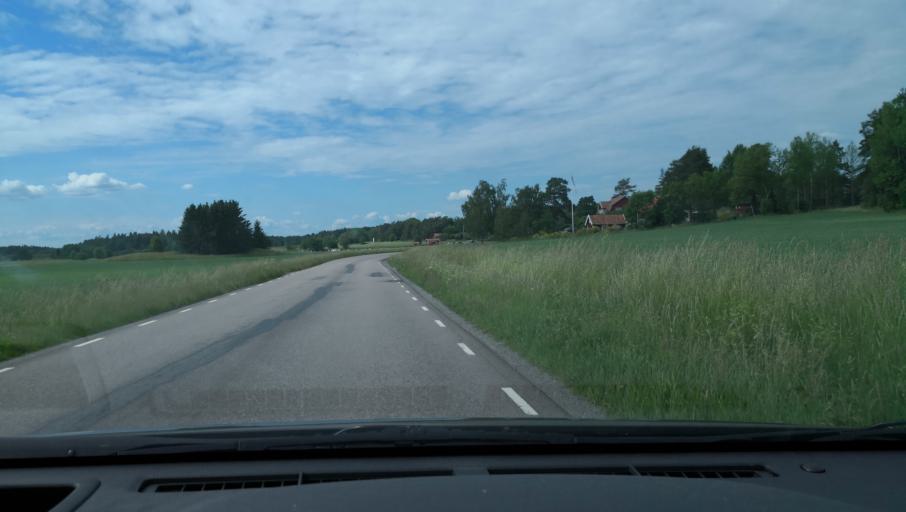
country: SE
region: Uppsala
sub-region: Uppsala Kommun
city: Uppsala
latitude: 59.8147
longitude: 17.5016
